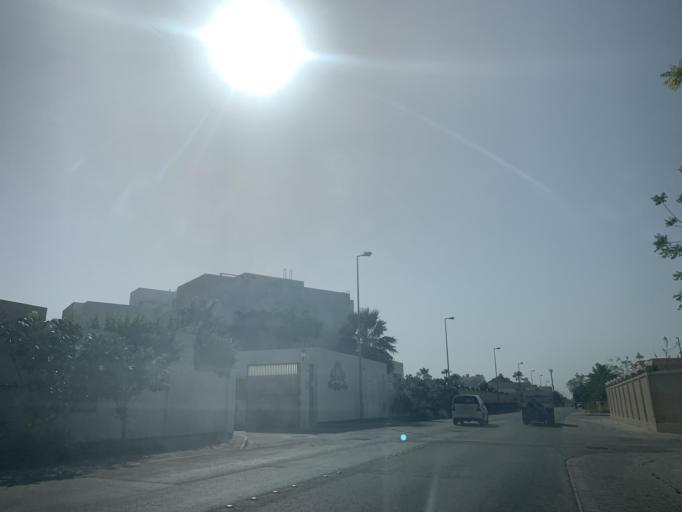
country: BH
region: Northern
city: Madinat `Isa
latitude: 26.1657
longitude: 50.5762
